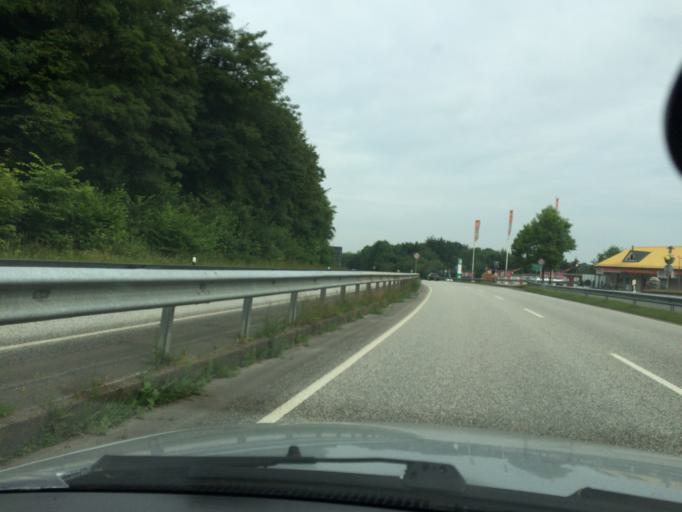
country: DK
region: South Denmark
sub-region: Aabenraa Kommune
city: Krusa
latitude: 54.8343
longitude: 9.4132
